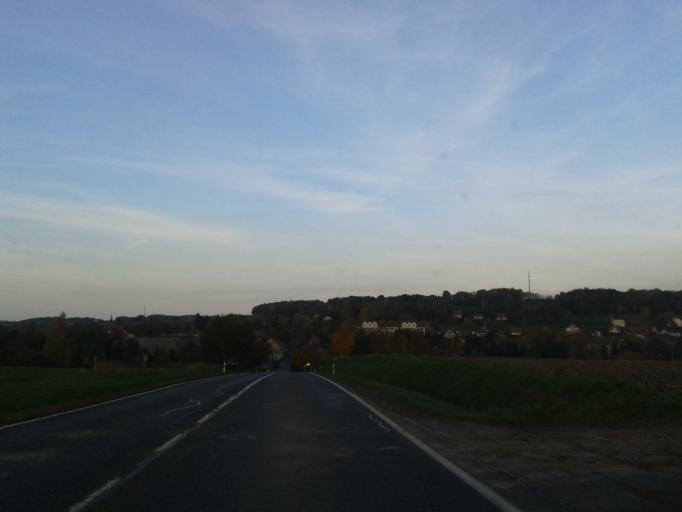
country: DE
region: Saxony
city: Niederschona
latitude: 50.9589
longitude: 13.4213
